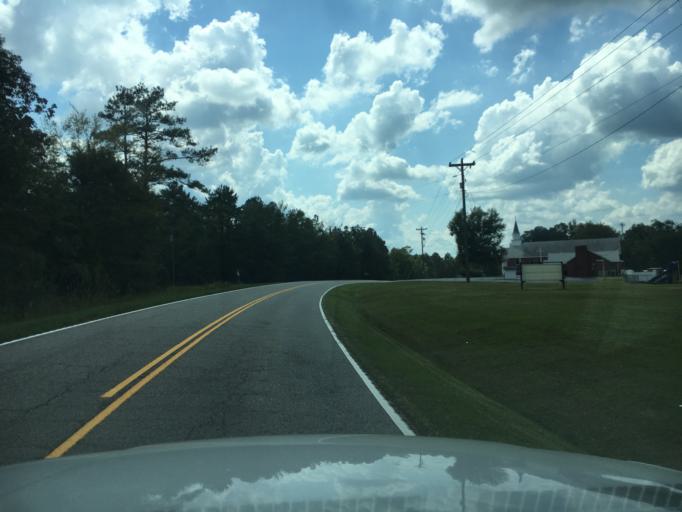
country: US
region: South Carolina
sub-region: Greenwood County
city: Greenwood
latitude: 34.0842
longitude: -82.1325
